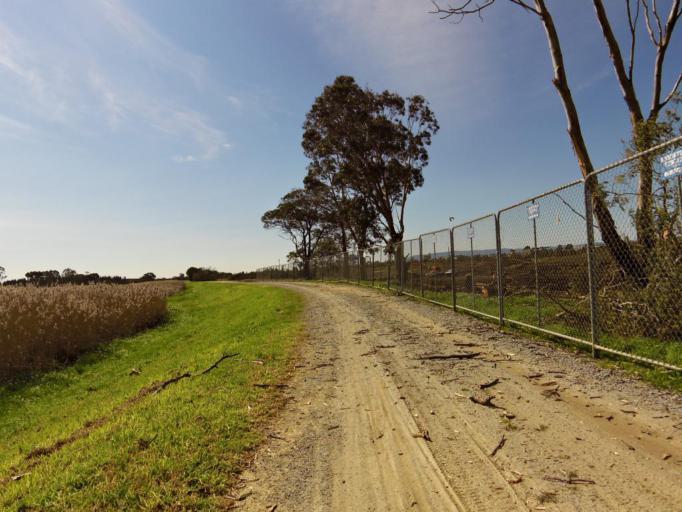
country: AU
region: Victoria
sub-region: Greater Dandenong
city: Keysborough
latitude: -38.0305
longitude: 145.1860
